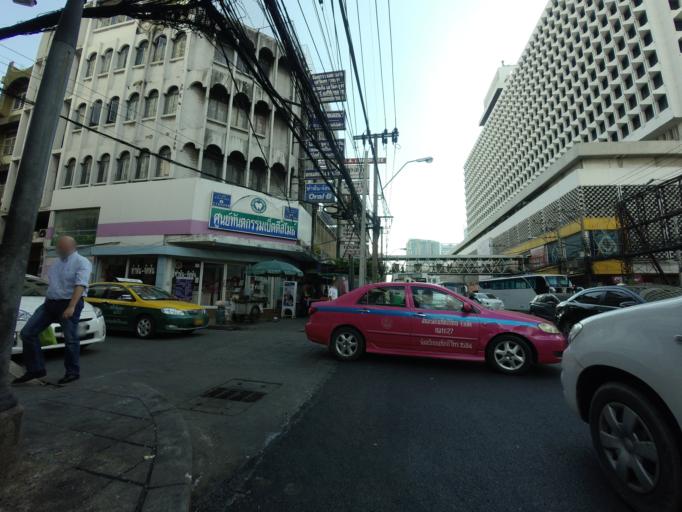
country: TH
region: Bangkok
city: Ratchathewi
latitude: 13.7539
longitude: 100.5420
